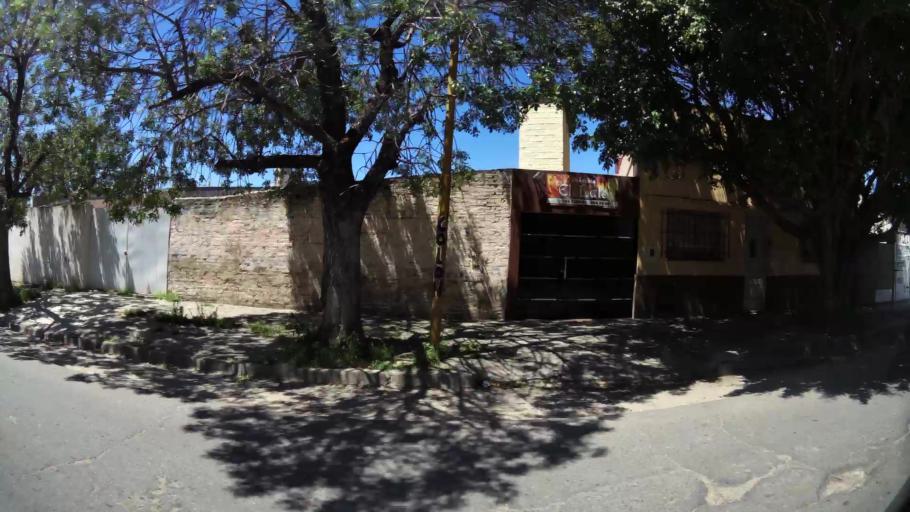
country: AR
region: Santa Fe
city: Santa Fe de la Vera Cruz
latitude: -31.6159
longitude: -60.7118
